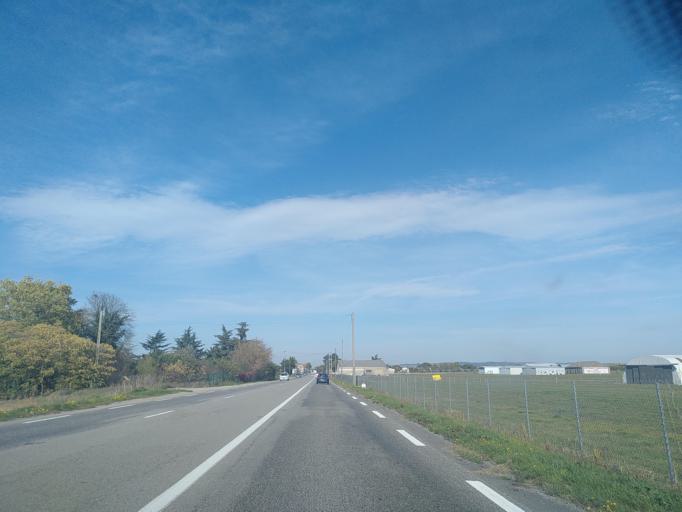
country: FR
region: Rhone-Alpes
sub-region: Departement de la Drome
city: Andancette
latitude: 45.2527
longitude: 4.8222
